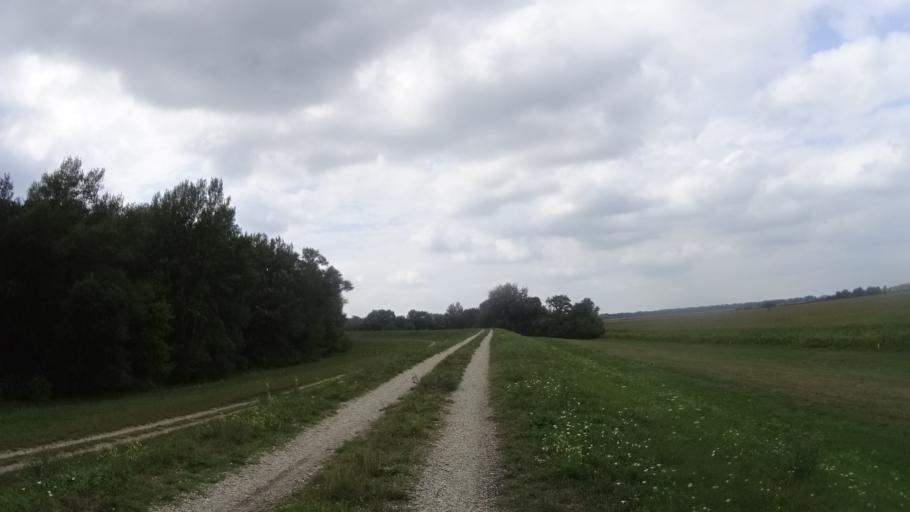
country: SK
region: Trnavsky
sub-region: Okres Dunajska Streda
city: Velky Meder
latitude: 47.7541
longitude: 17.7724
